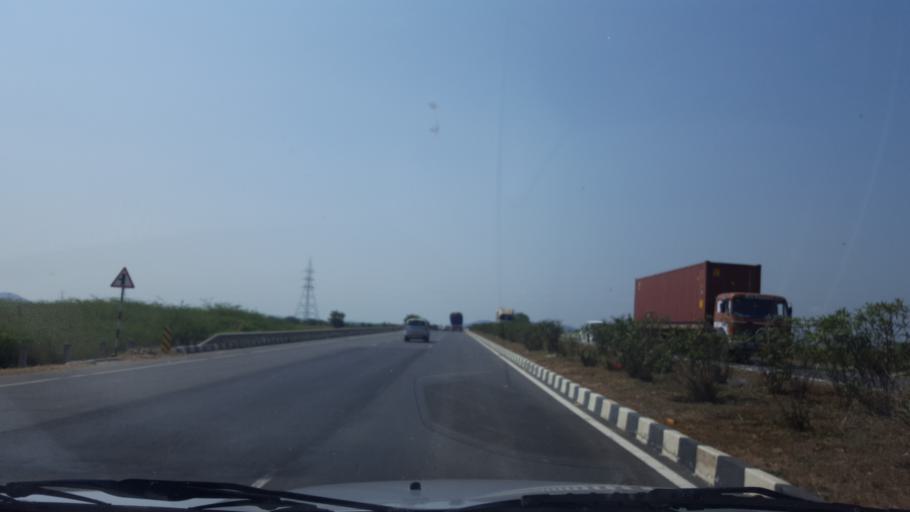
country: IN
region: Andhra Pradesh
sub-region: Guntur
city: Chilakalurupet
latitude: 16.0258
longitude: 80.1268
